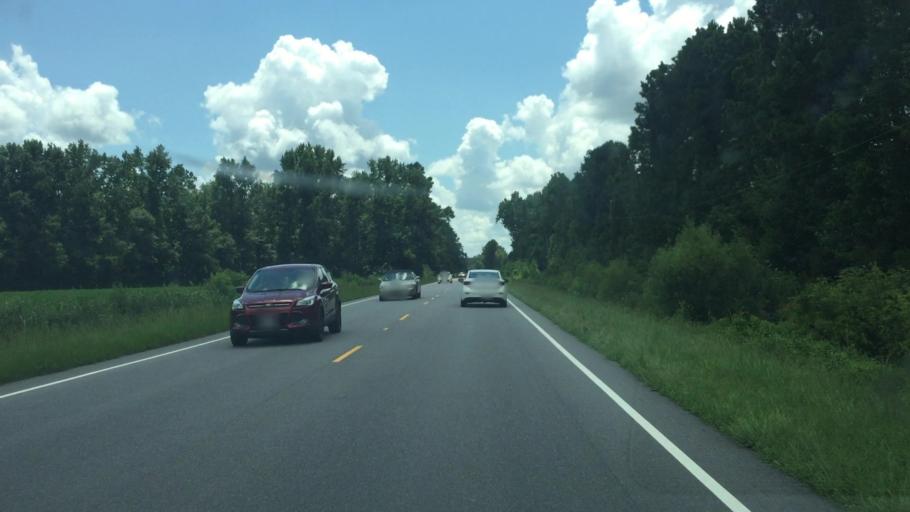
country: US
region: North Carolina
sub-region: Columbus County
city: Tabor City
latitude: 34.1931
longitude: -78.8360
